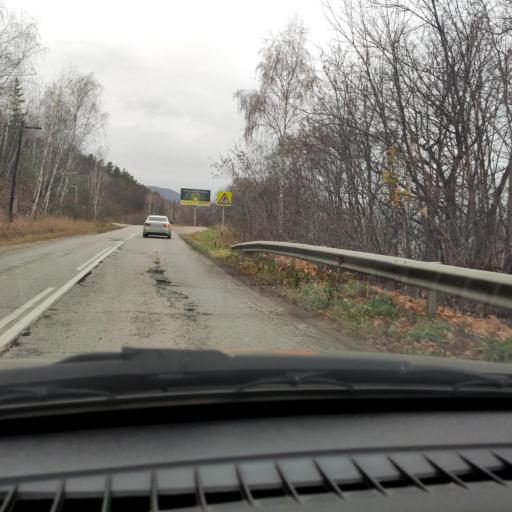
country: RU
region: Samara
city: Pribrezhnyy
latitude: 53.4402
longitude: 49.7515
